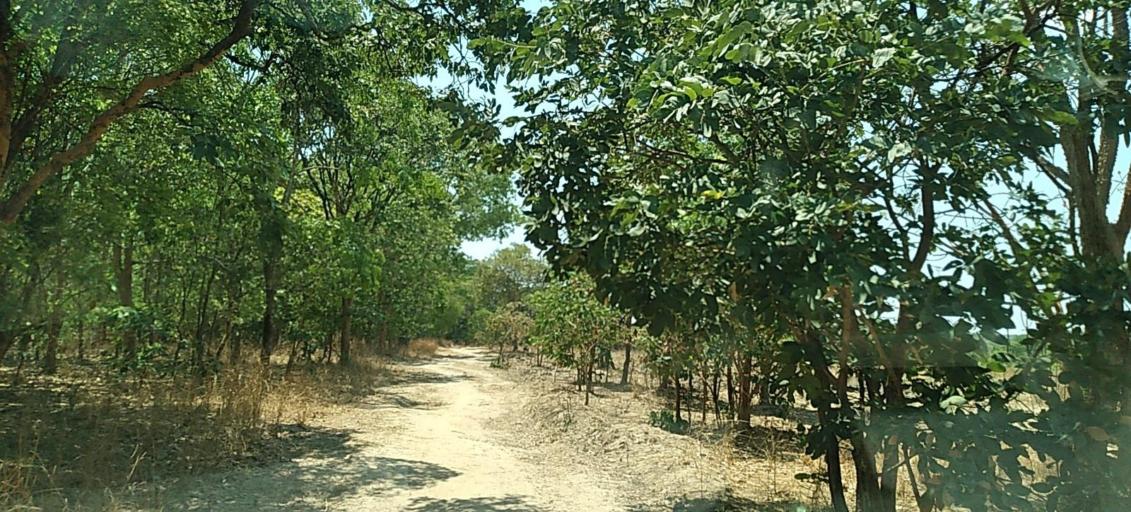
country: ZM
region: Central
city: Kapiri Mposhi
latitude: -13.6697
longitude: 28.4966
